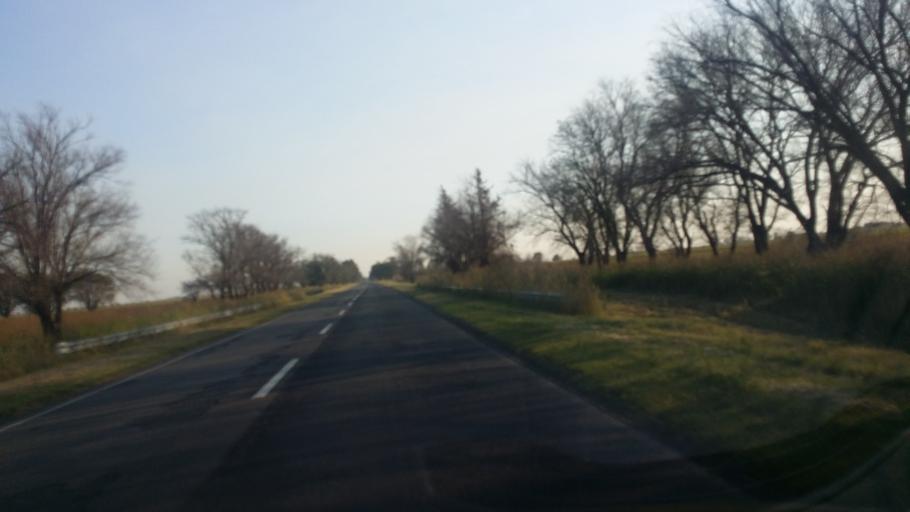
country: AR
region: La Pampa
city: Winifreda
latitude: -36.1947
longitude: -64.2782
